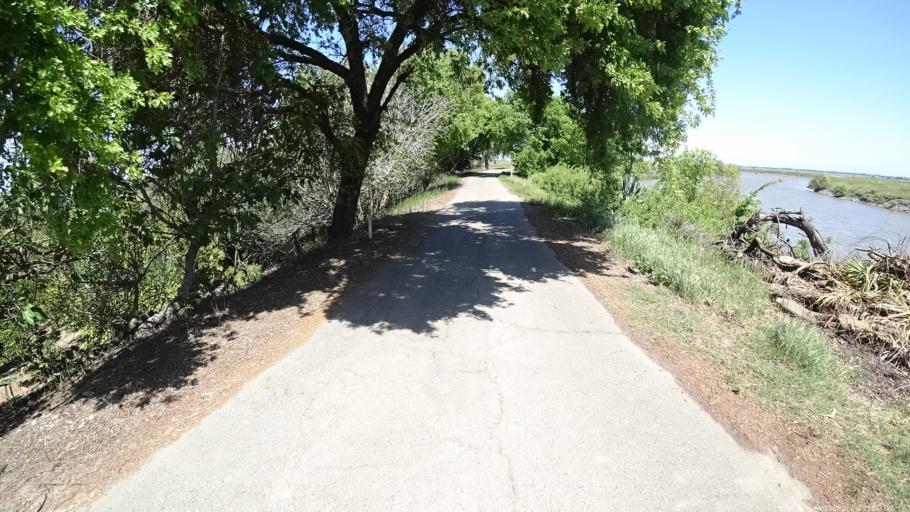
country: US
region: California
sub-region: Sacramento County
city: Walnut Grove
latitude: 38.2619
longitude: -121.5946
